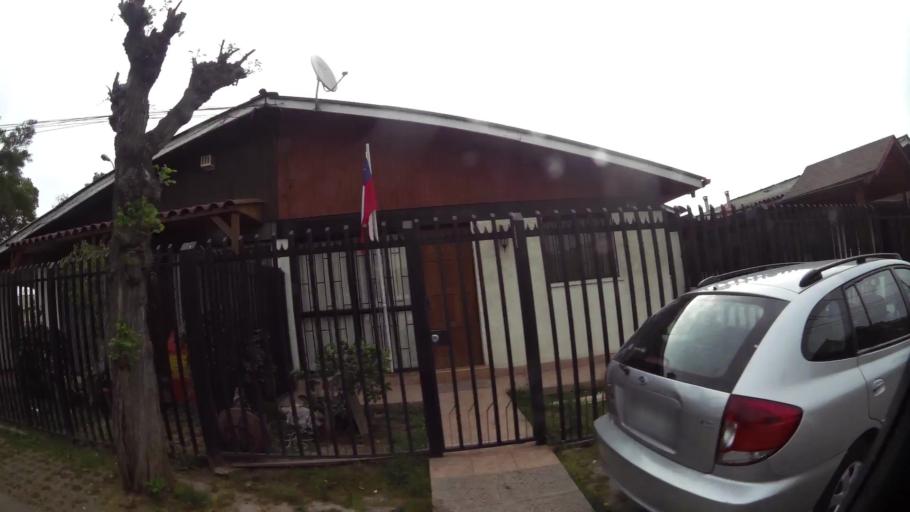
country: CL
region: Santiago Metropolitan
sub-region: Provincia de Santiago
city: Lo Prado
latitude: -33.5229
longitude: -70.7718
